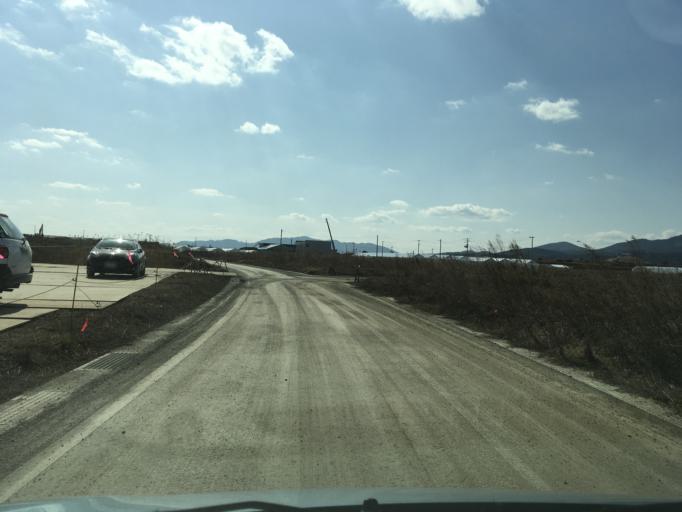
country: JP
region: Iwate
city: Ofunato
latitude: 38.8279
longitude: 141.5933
